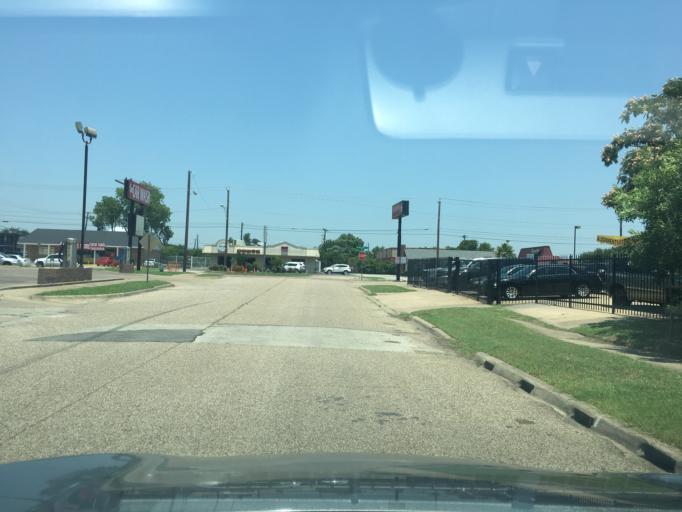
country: US
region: Texas
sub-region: Dallas County
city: Garland
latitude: 32.9162
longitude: -96.6878
